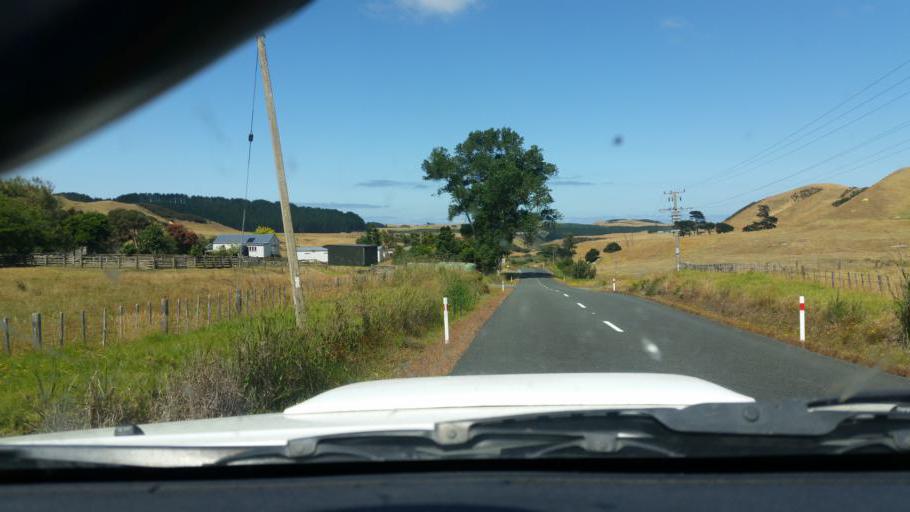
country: NZ
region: Northland
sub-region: Kaipara District
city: Dargaville
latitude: -35.8221
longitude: 173.6823
